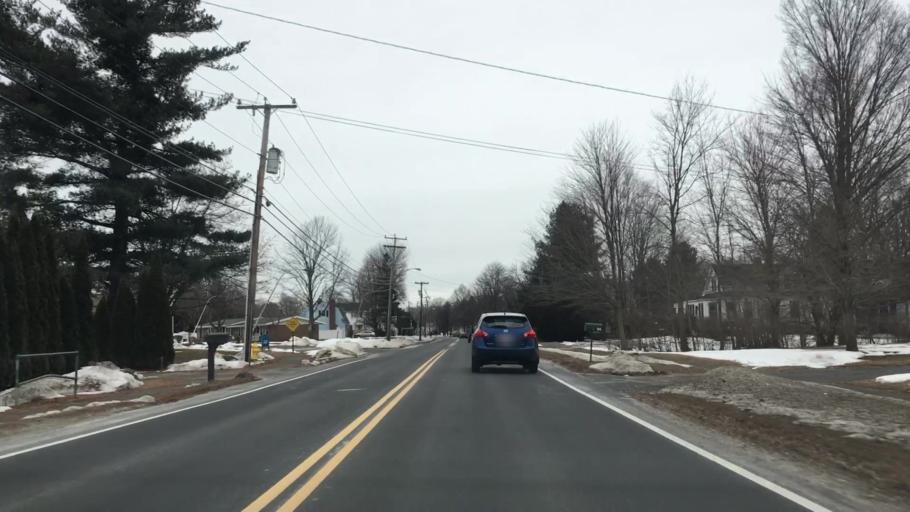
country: US
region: Massachusetts
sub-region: Hampden County
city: Agawam
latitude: 42.0698
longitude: -72.6785
